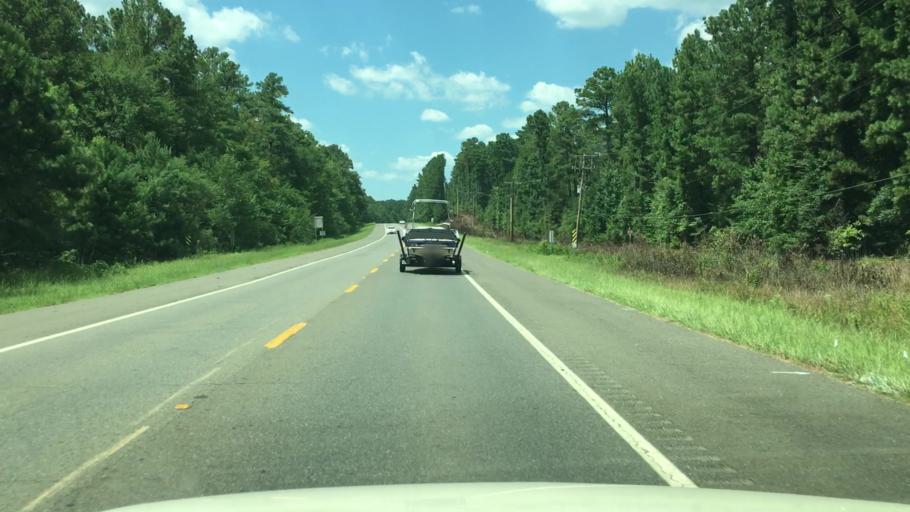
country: US
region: Arkansas
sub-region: Clark County
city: Arkadelphia
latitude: 34.1935
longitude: -93.0743
